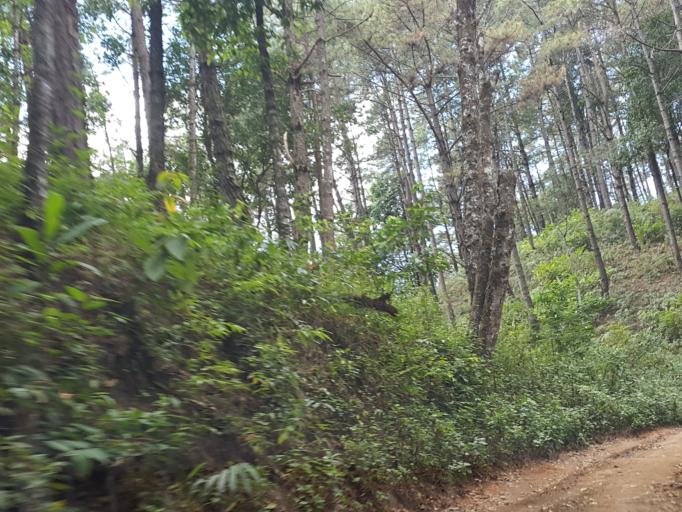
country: TH
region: Chiang Mai
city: Wiang Haeng
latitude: 19.5509
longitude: 98.8152
